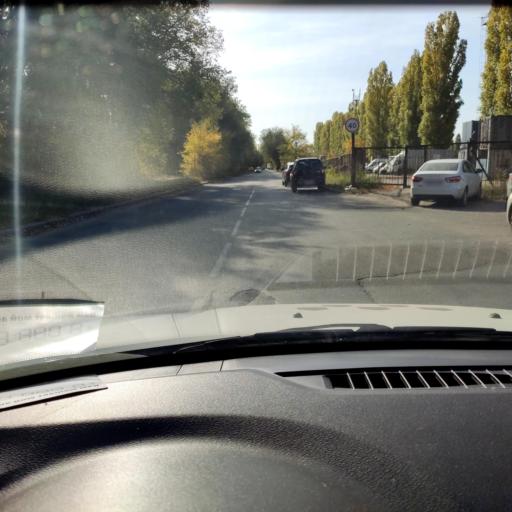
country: RU
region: Samara
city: Tol'yatti
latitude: 53.5553
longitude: 49.3093
